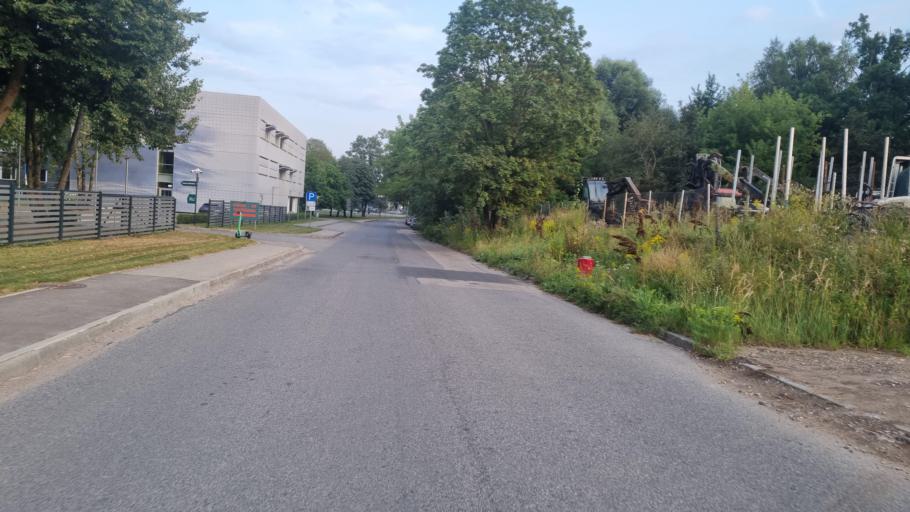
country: LV
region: Kekava
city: Balozi
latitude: 56.9101
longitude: 24.1506
